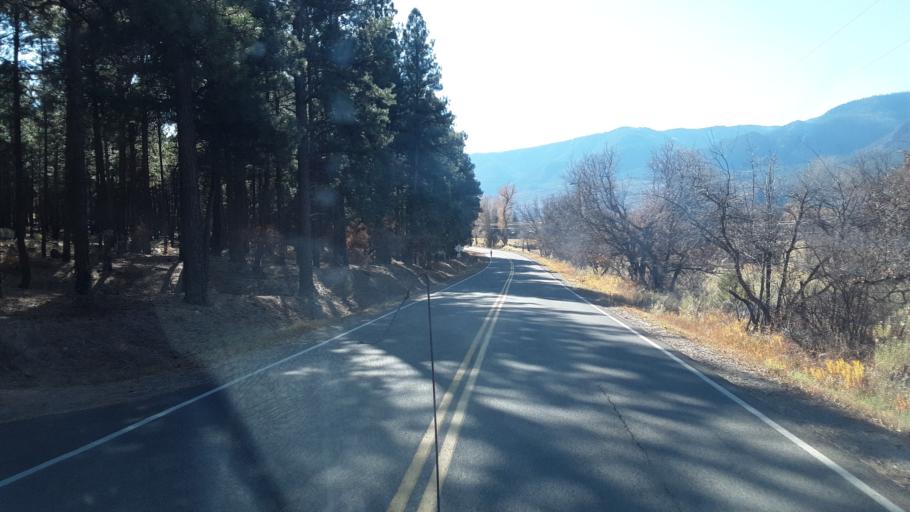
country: US
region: Colorado
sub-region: La Plata County
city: Durango
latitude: 37.4009
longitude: -107.8175
